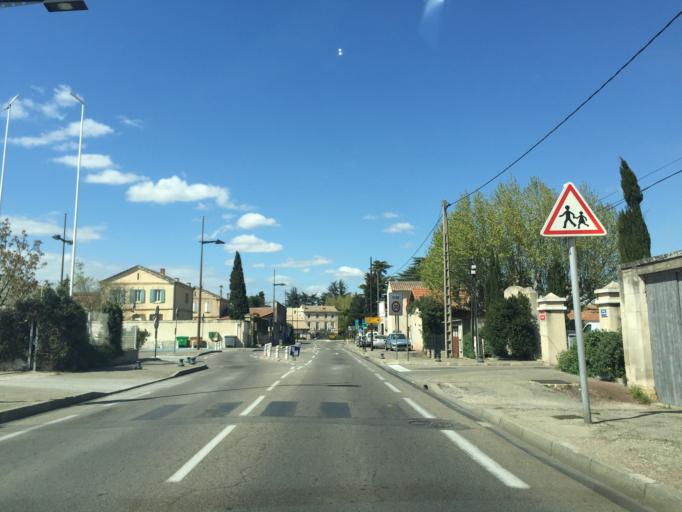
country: FR
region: Provence-Alpes-Cote d'Azur
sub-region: Departement du Vaucluse
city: Le Pontet
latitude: 43.9591
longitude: 4.8576
